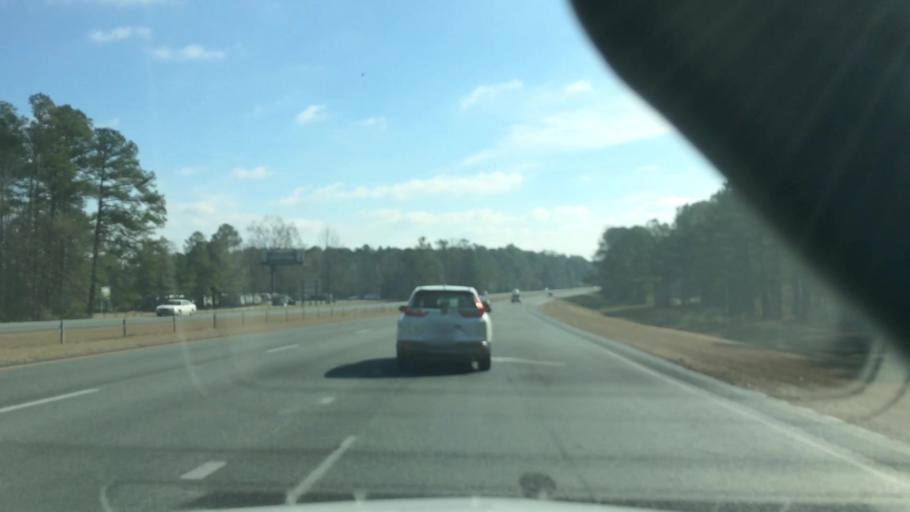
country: US
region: North Carolina
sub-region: Duplin County
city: Wallace
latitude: 34.7510
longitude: -77.9470
